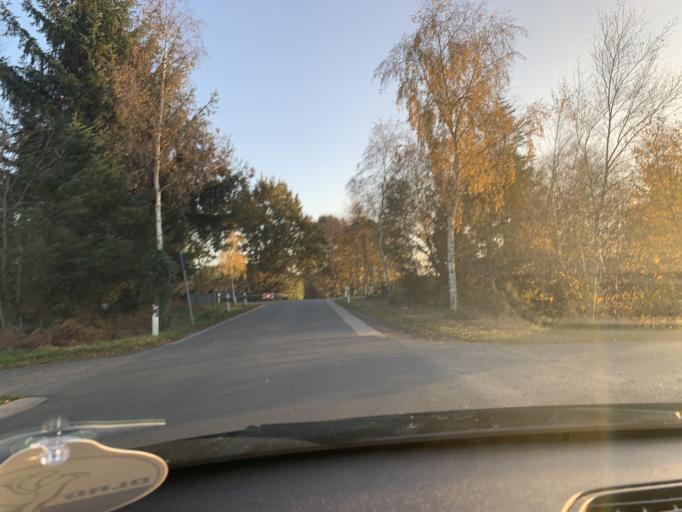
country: DE
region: Lower Saxony
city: Bad Zwischenahn
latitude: 53.1454
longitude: 8.0527
